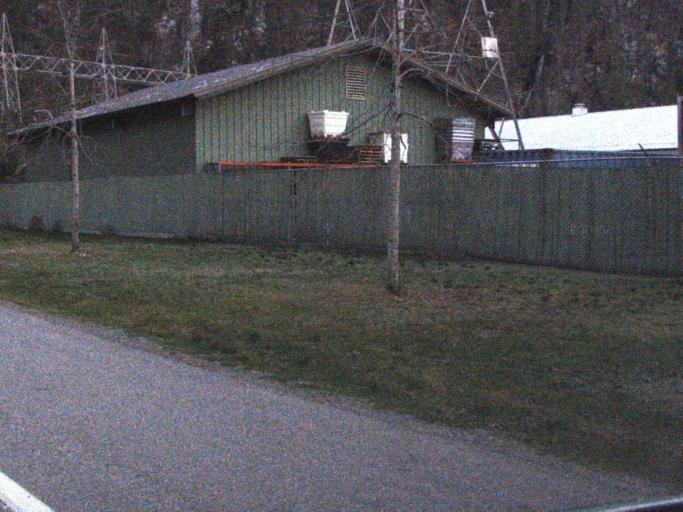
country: US
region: Washington
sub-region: Snohomish County
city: Darrington
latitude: 48.6744
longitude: -121.2443
